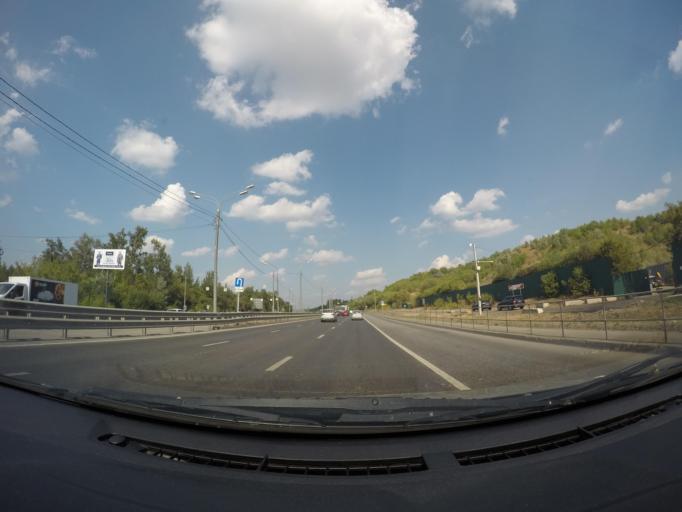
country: RU
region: Moskovskaya
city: Levoberezhnaya
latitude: 55.9027
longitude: 37.4915
